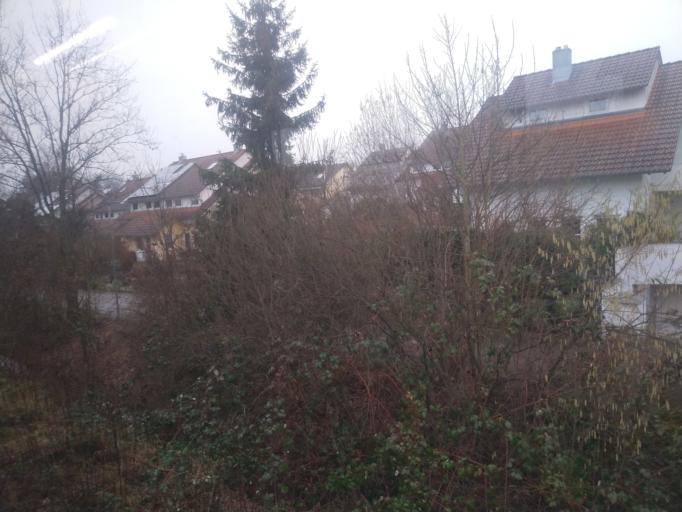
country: DE
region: Baden-Wuerttemberg
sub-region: Tuebingen Region
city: Uhldingen-Muhlhofen
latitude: 47.7371
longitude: 9.2485
